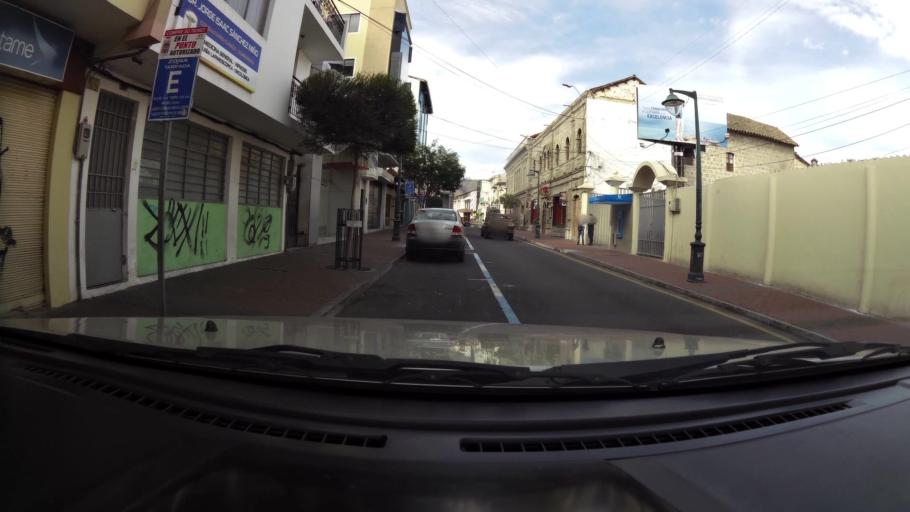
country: EC
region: Tungurahua
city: Ambato
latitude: -1.2337
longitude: -78.6278
